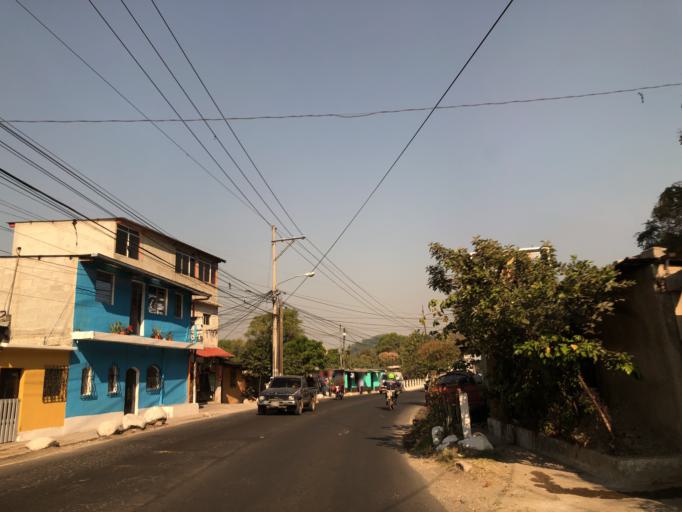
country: GT
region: Guatemala
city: Villa Canales
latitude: 14.4874
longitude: -90.5345
